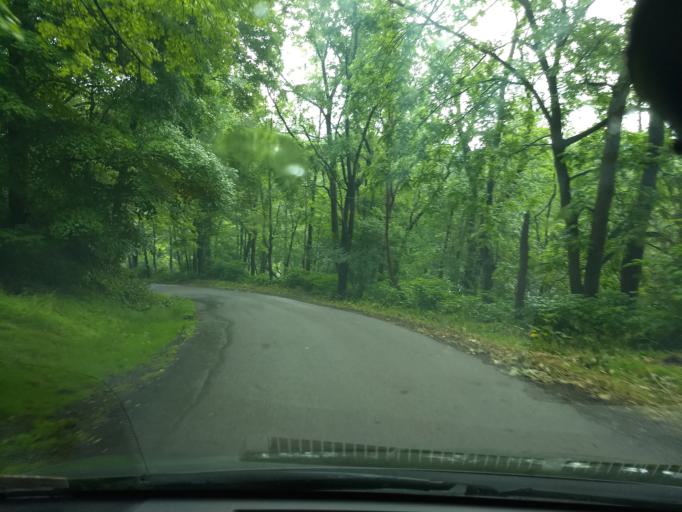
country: US
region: Pennsylvania
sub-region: Westmoreland County
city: Avonmore
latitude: 40.5268
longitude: -79.4962
